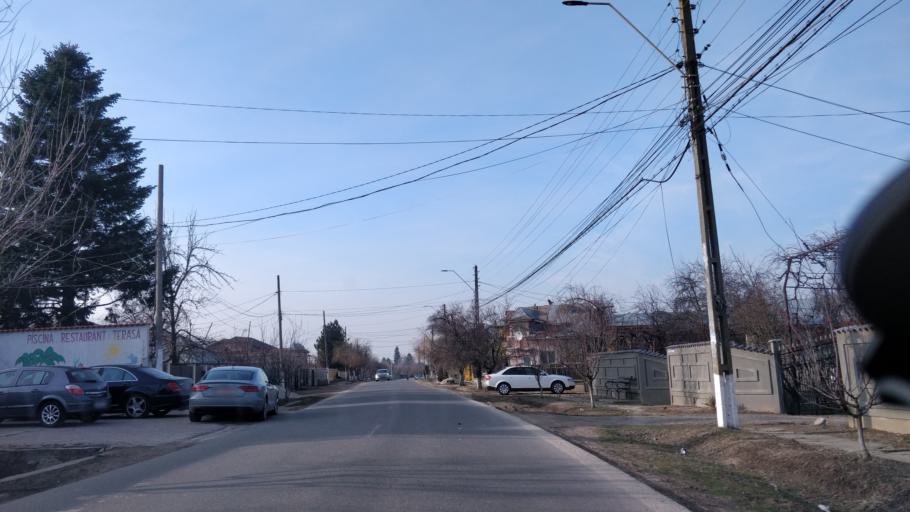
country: RO
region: Giurgiu
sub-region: Comuna Ulmi
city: Ulmi
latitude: 44.4947
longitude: 25.7748
